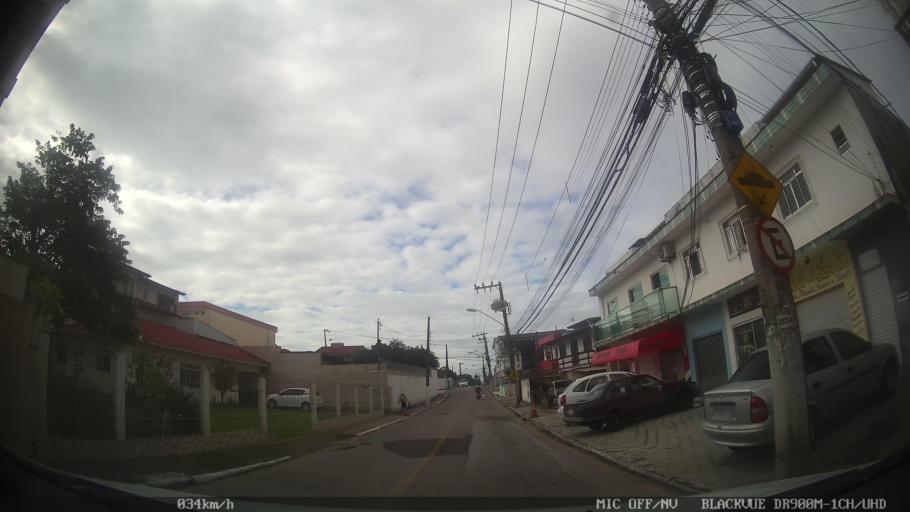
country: BR
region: Santa Catarina
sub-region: Sao Jose
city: Campinas
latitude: -27.5780
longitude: -48.6214
